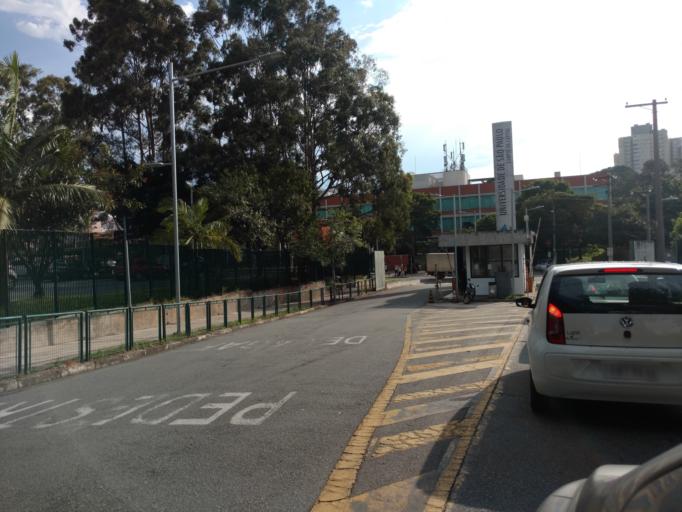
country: BR
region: Sao Paulo
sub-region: Osasco
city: Osasco
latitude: -23.5690
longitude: -46.7408
